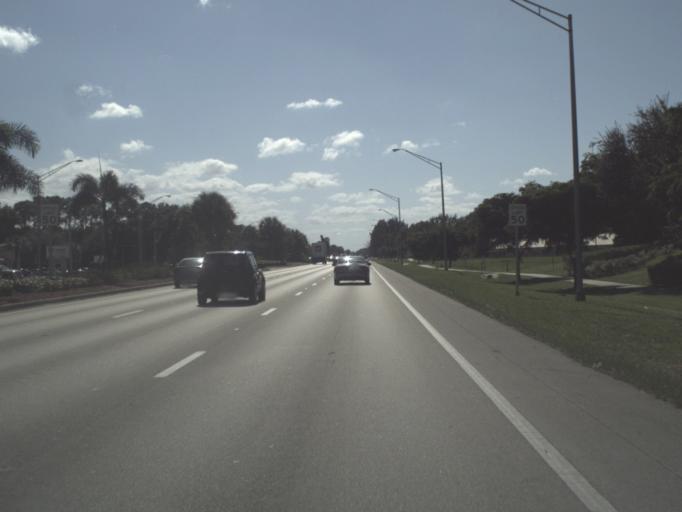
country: US
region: Florida
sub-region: Collier County
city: Naples Manor
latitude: 26.0909
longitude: -81.7333
